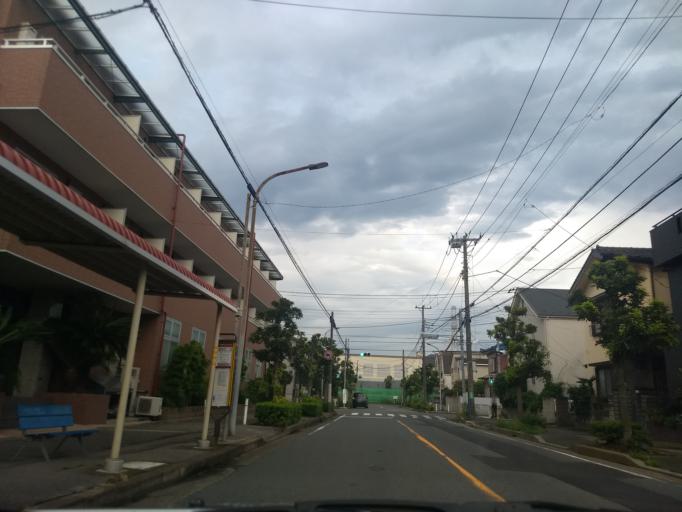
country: JP
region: Tokyo
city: Urayasu
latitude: 35.6852
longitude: 139.9313
